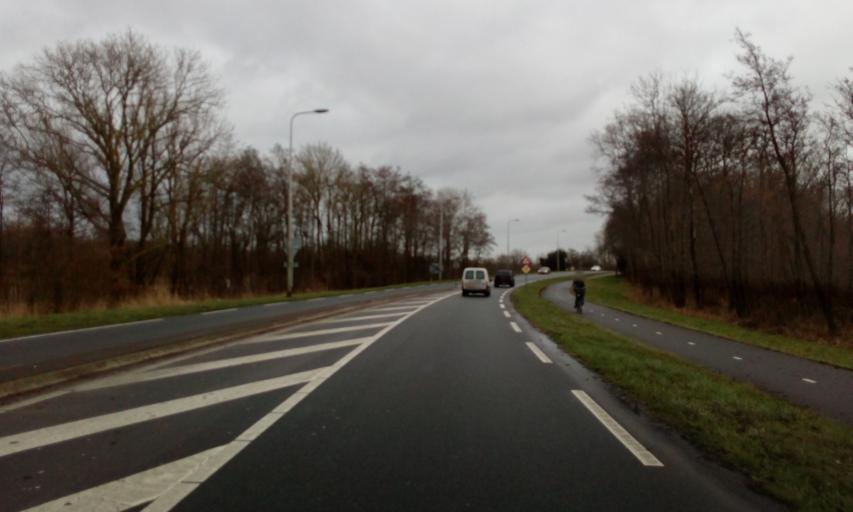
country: NL
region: Utrecht
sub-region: Stichtse Vecht
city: Vreeland
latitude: 52.2349
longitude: 5.0602
